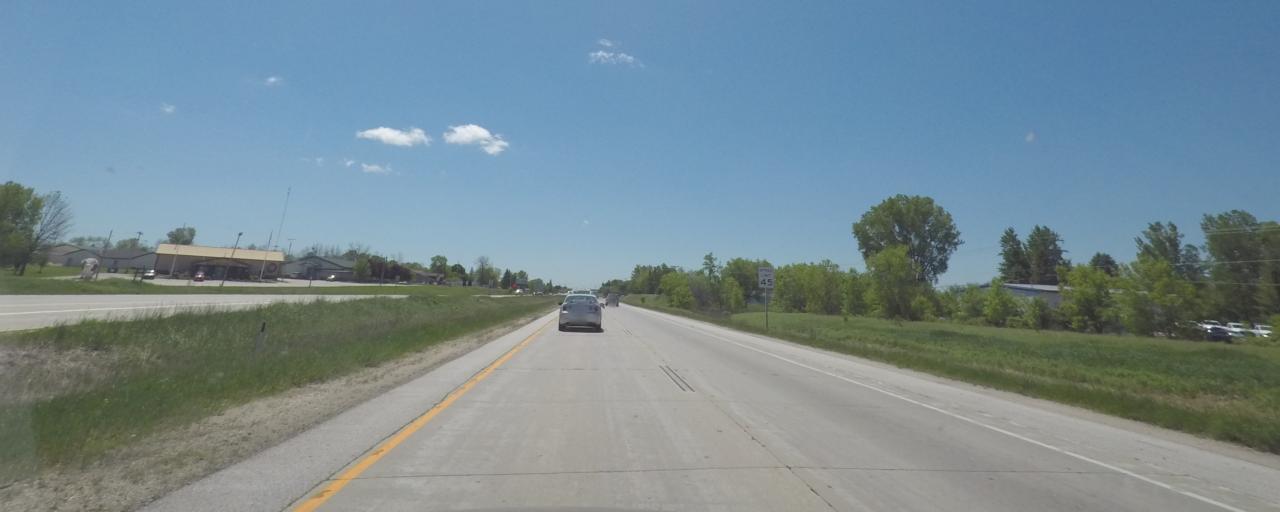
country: US
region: Wisconsin
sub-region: Sheboygan County
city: Plymouth
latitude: 43.7463
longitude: -87.9414
